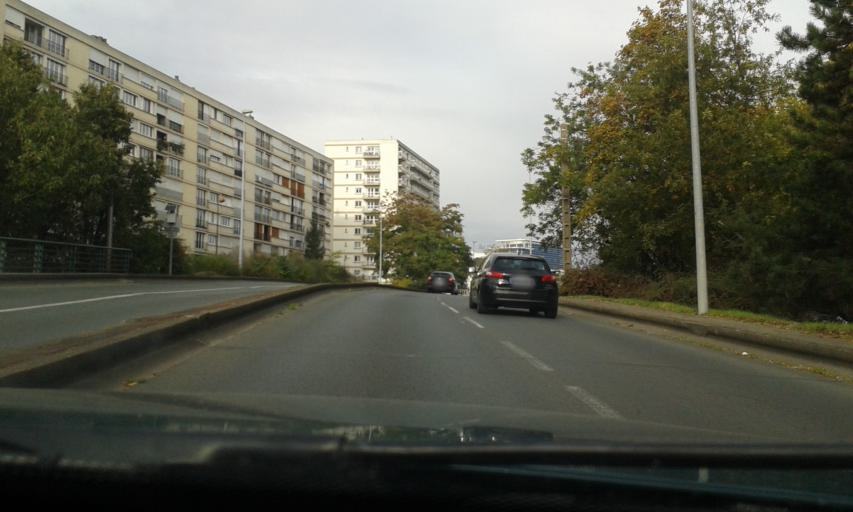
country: FR
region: Centre
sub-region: Departement du Loiret
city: Orleans
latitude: 47.8992
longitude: 1.8948
